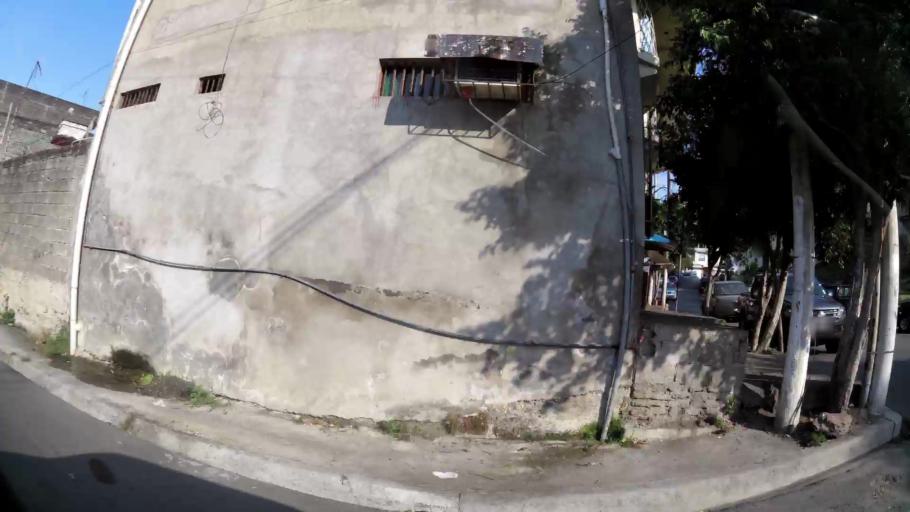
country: EC
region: Guayas
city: Guayaquil
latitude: -2.1578
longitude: -79.9119
